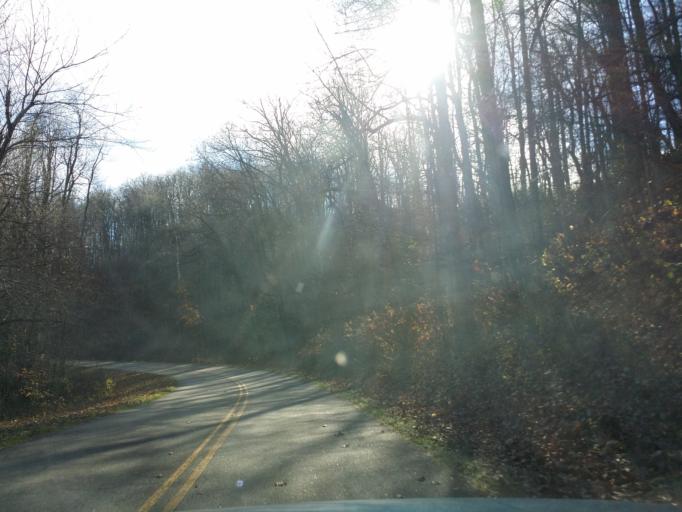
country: US
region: North Carolina
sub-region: McDowell County
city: West Marion
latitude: 35.7555
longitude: -82.1839
